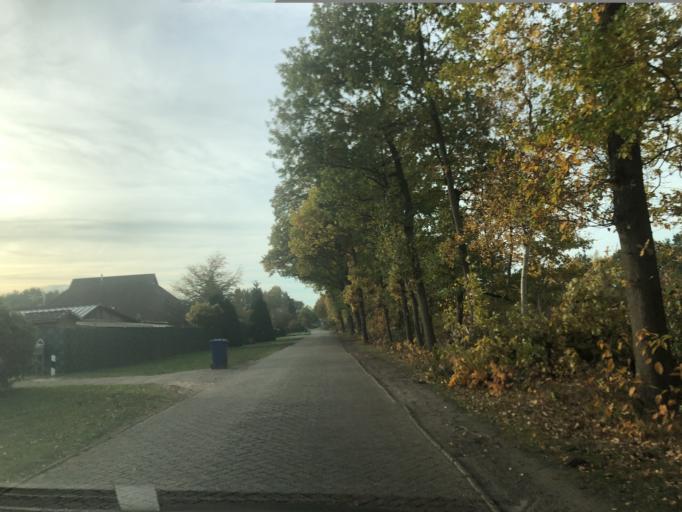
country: DE
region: Lower Saxony
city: Edewecht
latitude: 53.0894
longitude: 8.0679
